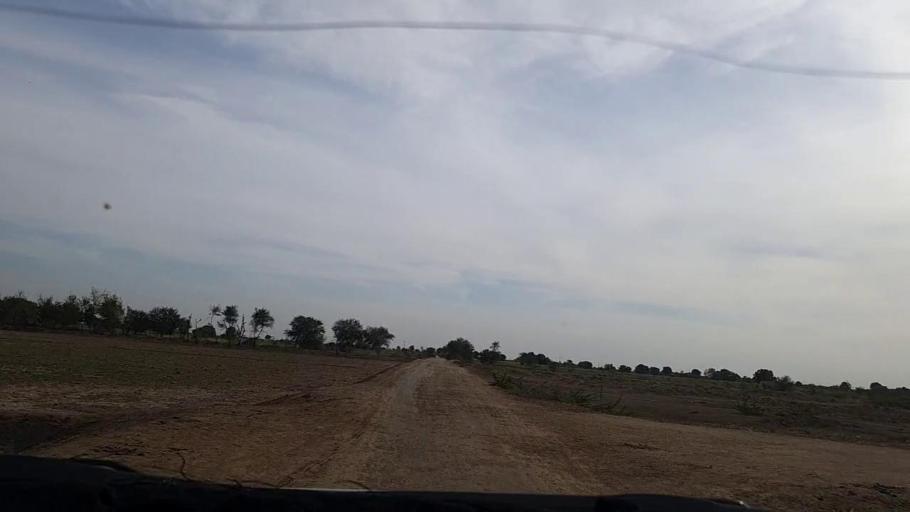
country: PK
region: Sindh
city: Dhoro Naro
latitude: 25.4090
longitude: 69.5181
